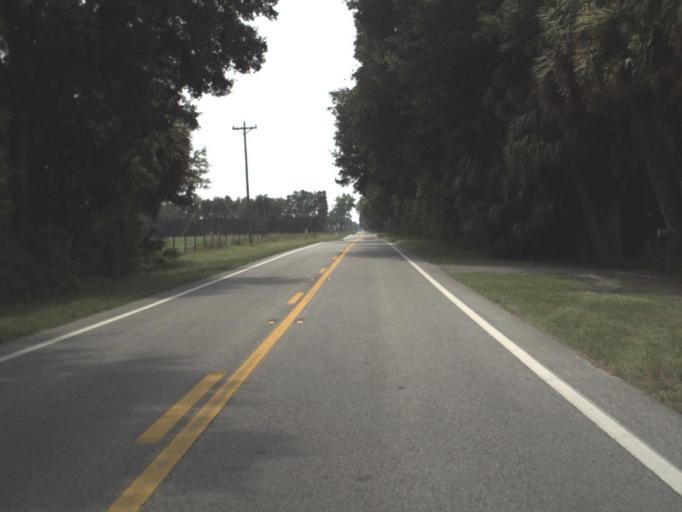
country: US
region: Florida
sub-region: Levy County
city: Chiefland
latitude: 29.4051
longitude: -82.8889
